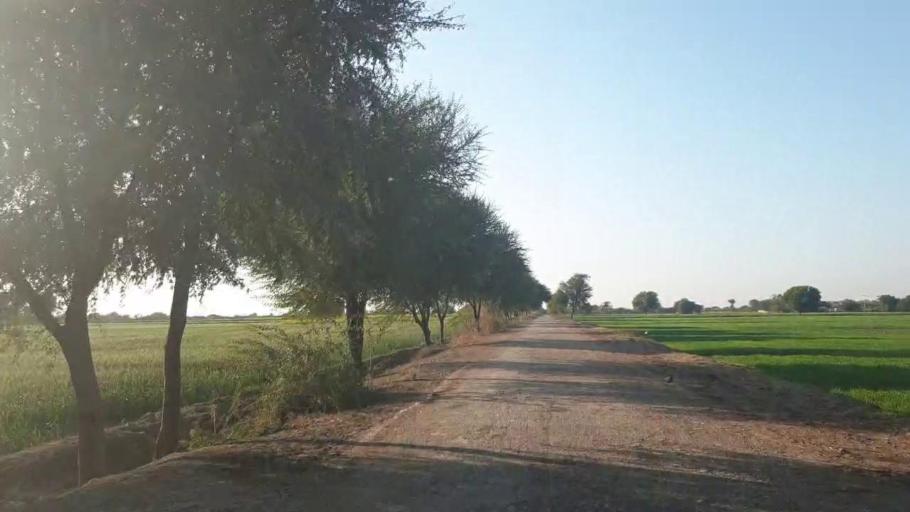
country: PK
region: Sindh
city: Shahpur Chakar
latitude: 26.0608
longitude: 68.6554
